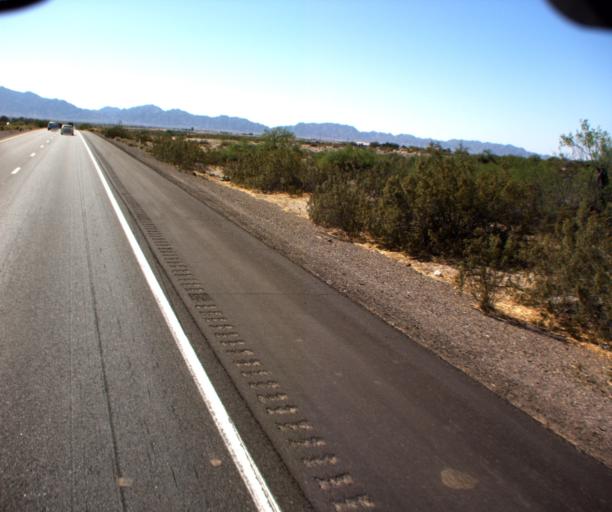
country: US
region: Arizona
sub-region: Yuma County
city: Wellton
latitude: 32.6556
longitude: -114.1695
